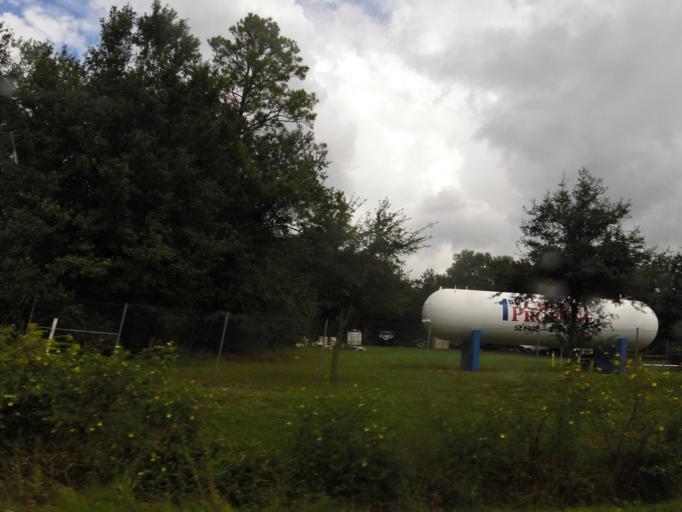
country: US
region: Florida
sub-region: Clay County
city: Middleburg
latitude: 30.0910
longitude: -81.9470
